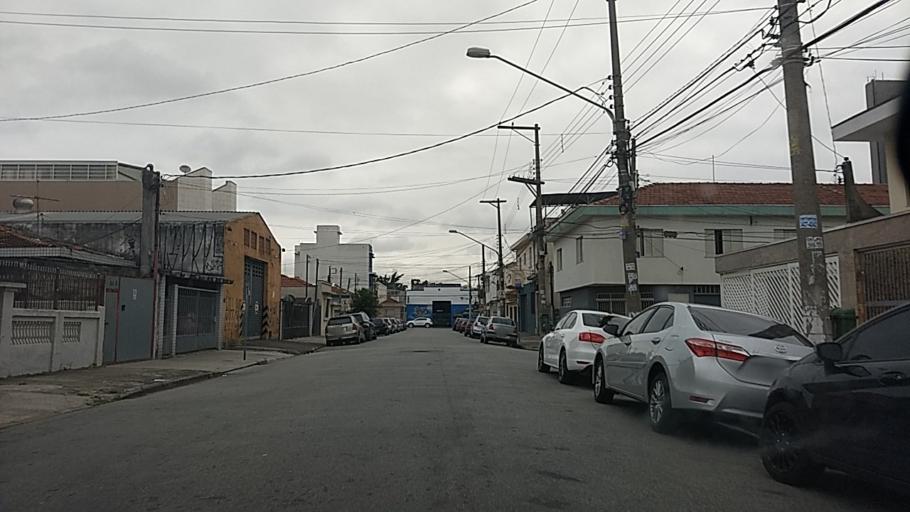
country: BR
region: Sao Paulo
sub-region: Sao Paulo
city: Sao Paulo
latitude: -23.5185
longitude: -46.5941
